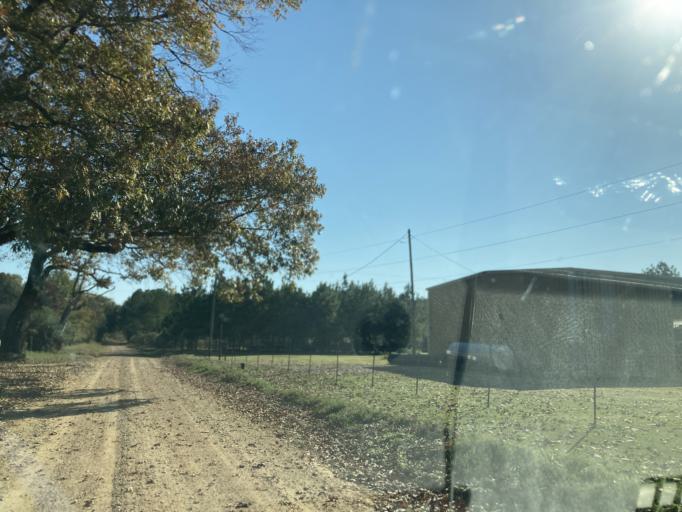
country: US
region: Mississippi
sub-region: Madison County
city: Kearney Park
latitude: 32.7167
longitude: -90.2943
